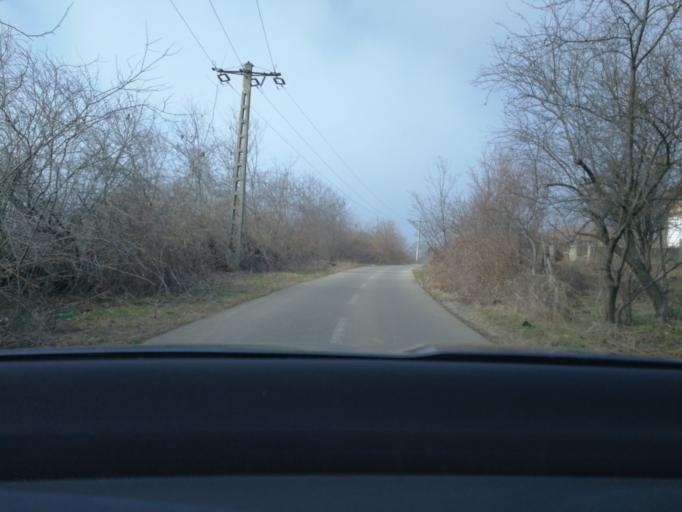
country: RO
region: Prahova
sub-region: Comuna Magureni
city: Lunca Prahovei
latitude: 45.0514
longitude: 25.7531
